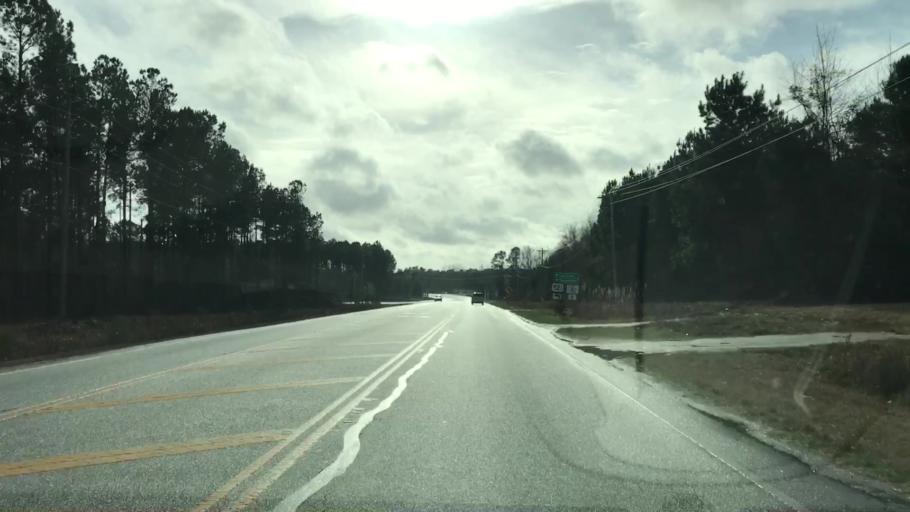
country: US
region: South Carolina
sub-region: Williamsburg County
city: Andrews
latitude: 33.4459
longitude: -79.5878
